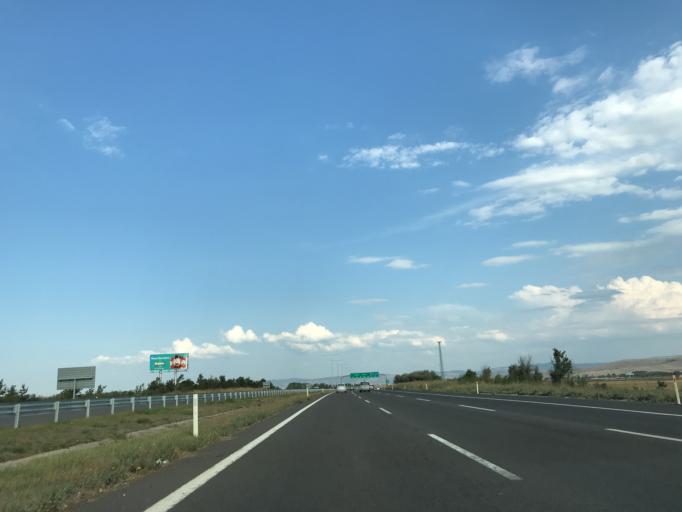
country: TR
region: Bolu
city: Dortdivan
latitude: 40.7457
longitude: 32.1083
